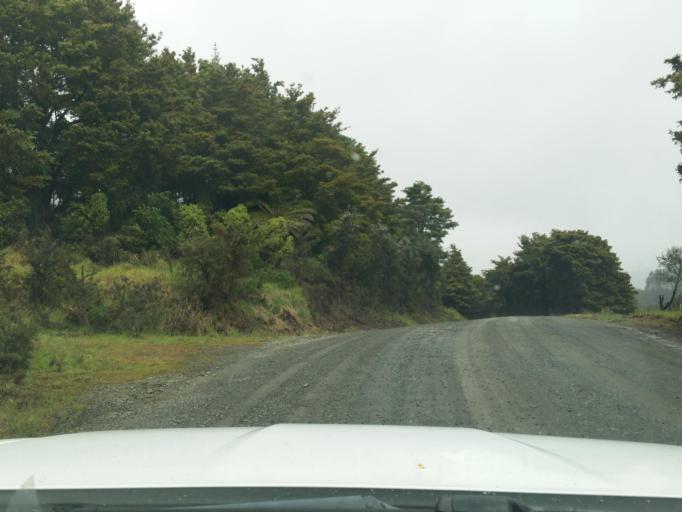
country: NZ
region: Northland
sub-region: Kaipara District
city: Dargaville
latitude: -35.7359
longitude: 173.9094
